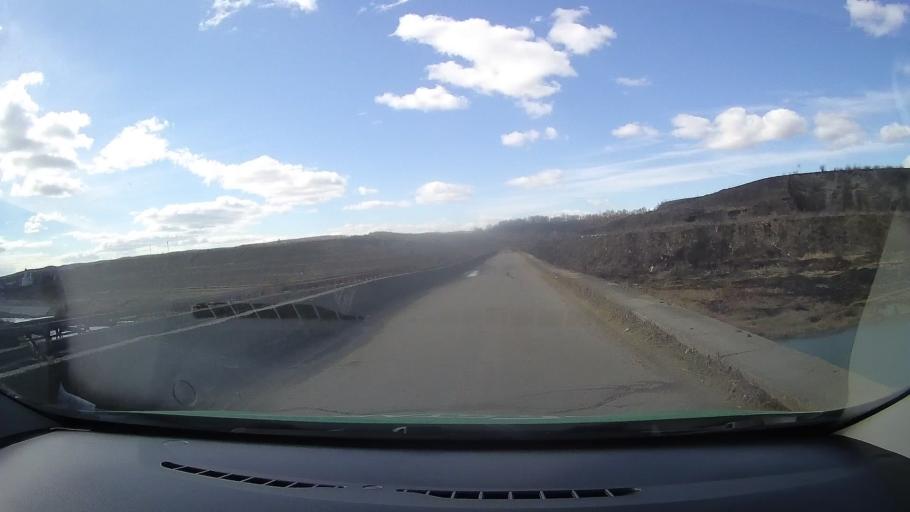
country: RO
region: Dambovita
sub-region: Comuna Doicesti
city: Doicesti
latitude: 44.9957
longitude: 25.3878
